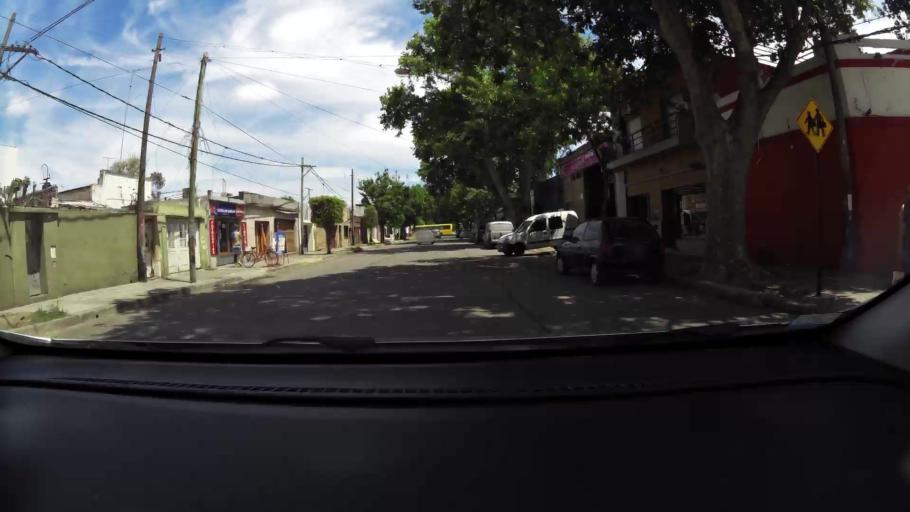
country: AR
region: Santa Fe
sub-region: Departamento de Rosario
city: Rosario
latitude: -32.9762
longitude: -60.6284
